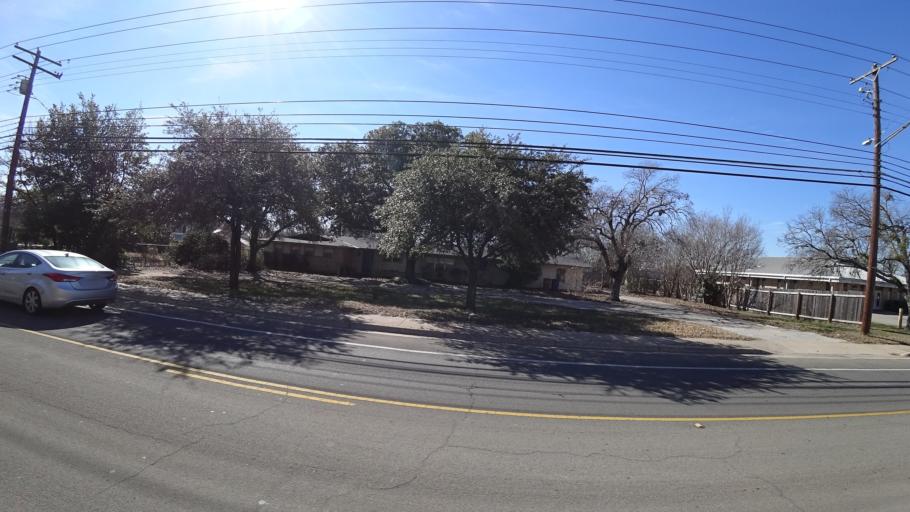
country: US
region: Texas
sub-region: Travis County
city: Wells Branch
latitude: 30.3847
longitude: -97.7022
